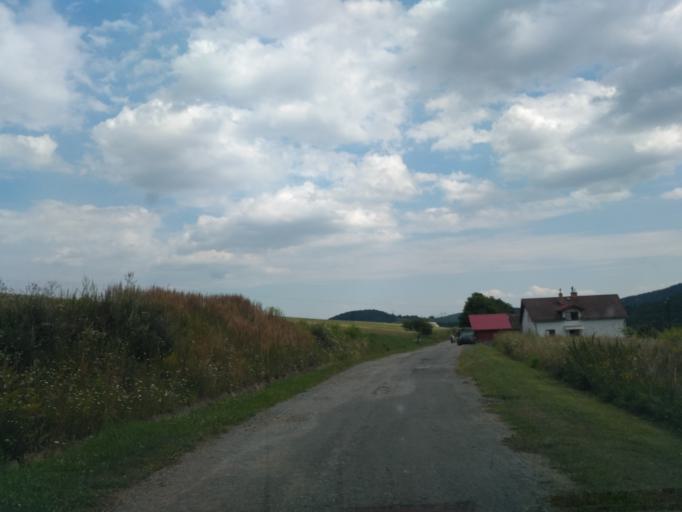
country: SK
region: Presovsky
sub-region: Okres Presov
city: Presov
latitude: 48.9161
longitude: 21.1721
